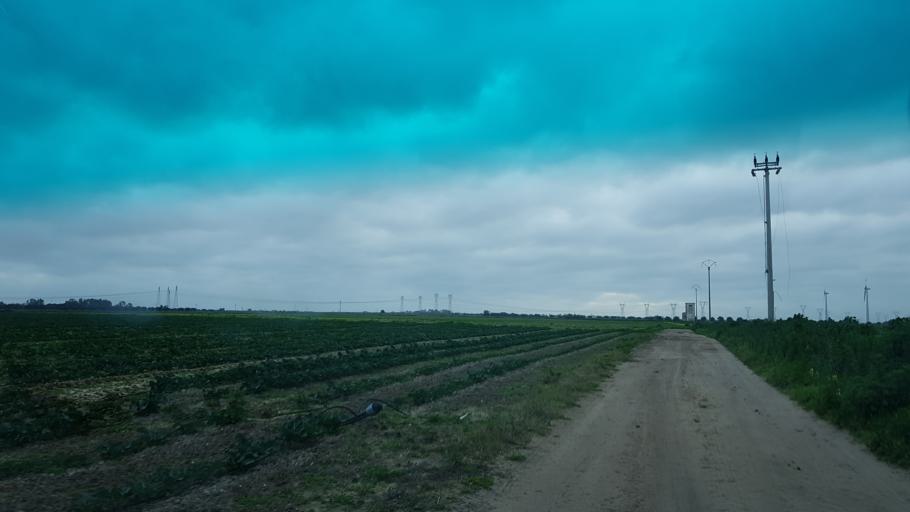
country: IT
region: Apulia
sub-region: Provincia di Brindisi
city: Tuturano
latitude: 40.5701
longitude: 17.9967
